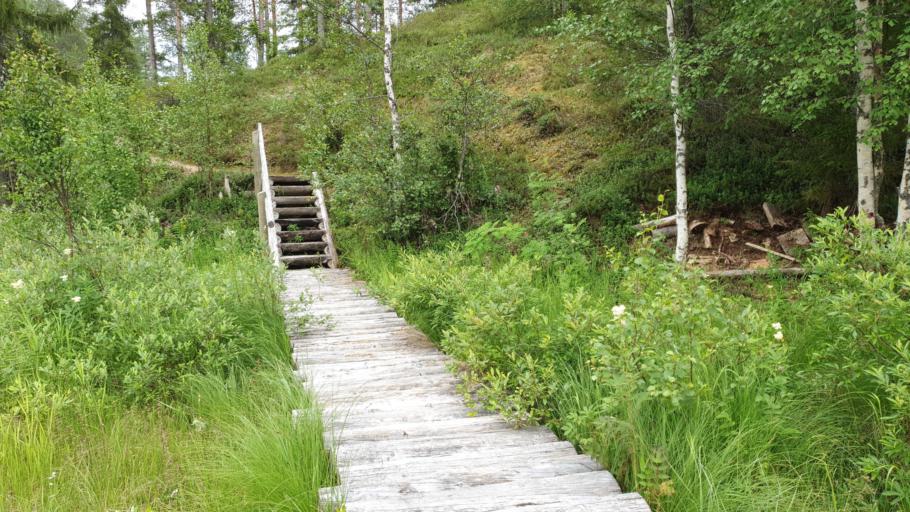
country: RU
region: Republic of Karelia
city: Kostomuksha
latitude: 64.7577
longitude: 30.0006
